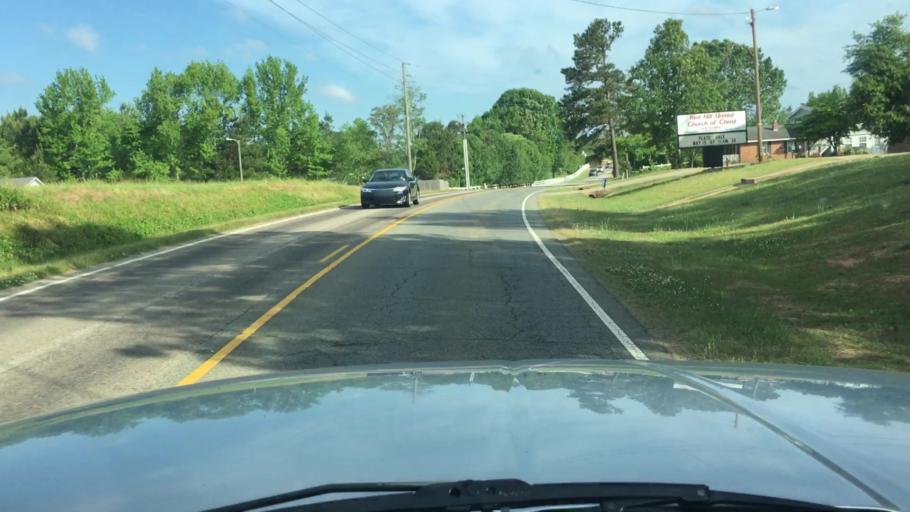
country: US
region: North Carolina
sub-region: Johnston County
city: Wilsons Mills
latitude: 35.6406
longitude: -78.3386
